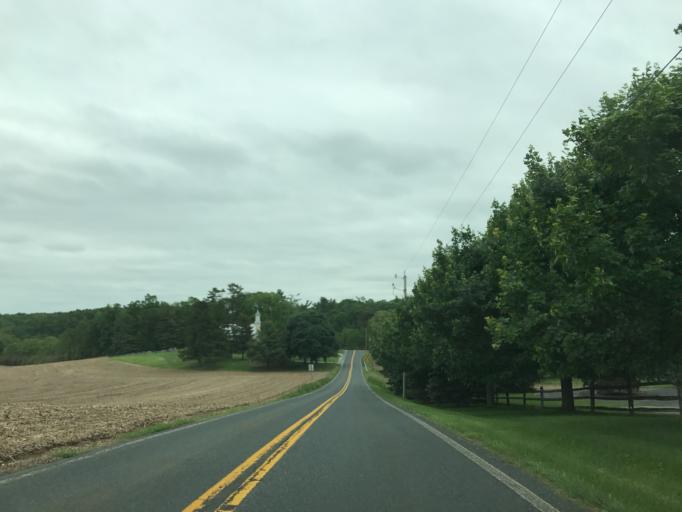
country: US
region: Maryland
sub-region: Carroll County
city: Hampstead
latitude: 39.5974
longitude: -76.8891
